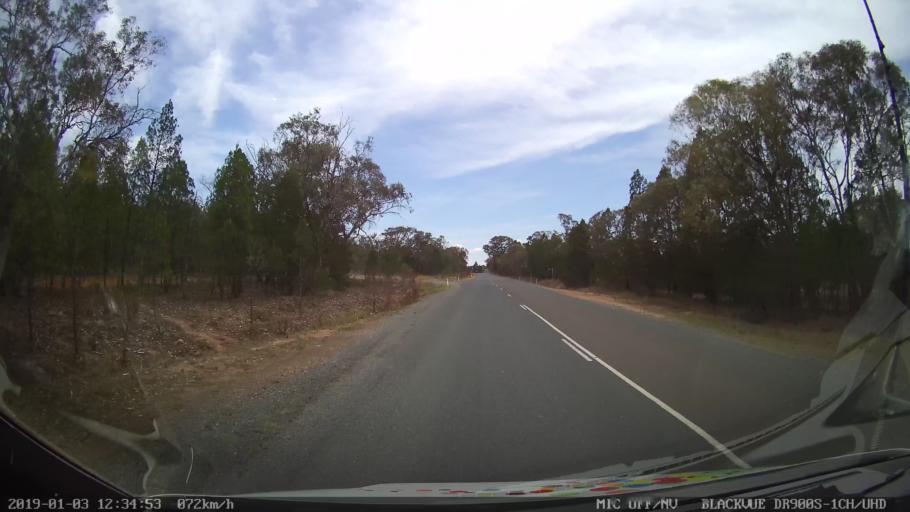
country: AU
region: New South Wales
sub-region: Weddin
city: Grenfell
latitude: -33.8720
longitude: 148.1670
